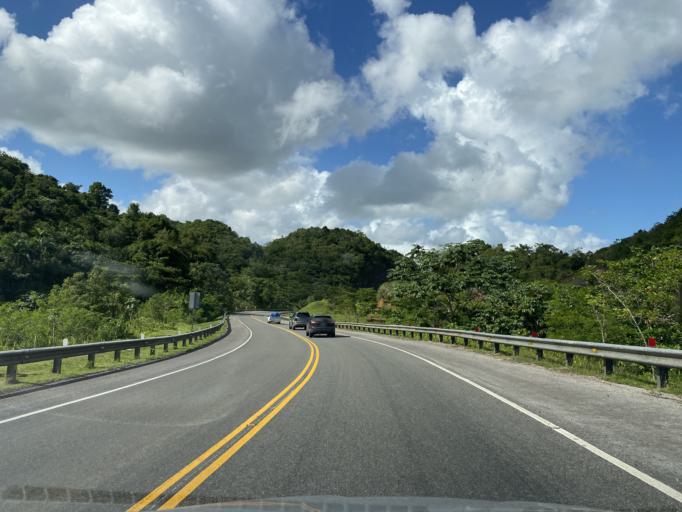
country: DO
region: Duarte
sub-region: Villa Riva
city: Agua Santa del Yuna
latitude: 19.1048
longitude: -69.8313
